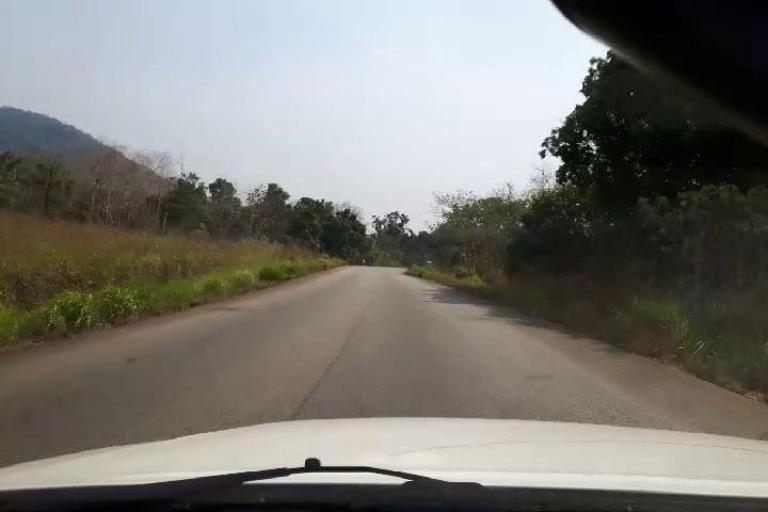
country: SL
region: Northern Province
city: Yonibana
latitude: 8.3815
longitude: -12.1990
